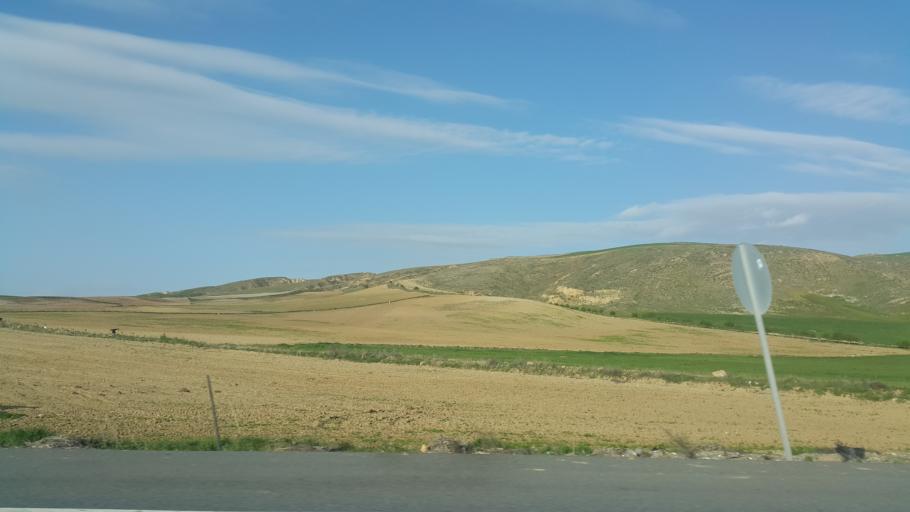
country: TR
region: Ankara
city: Sereflikochisar
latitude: 39.0537
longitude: 33.4333
